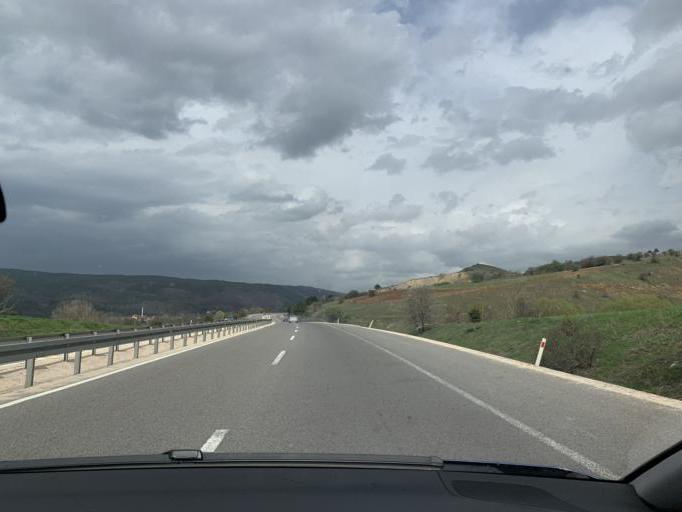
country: TR
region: Bolu
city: Yenicaga
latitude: 40.7826
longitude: 32.1022
